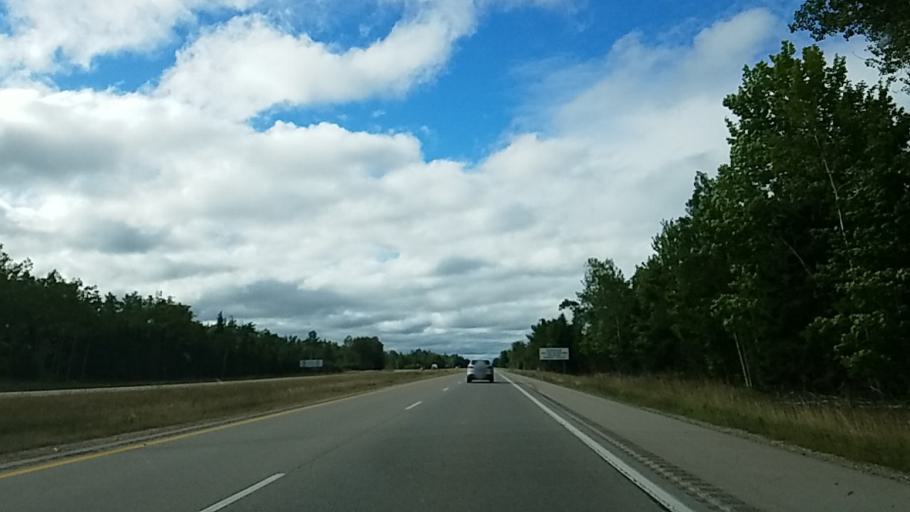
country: US
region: Michigan
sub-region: Mackinac County
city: Saint Ignace
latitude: 45.7466
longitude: -84.7289
